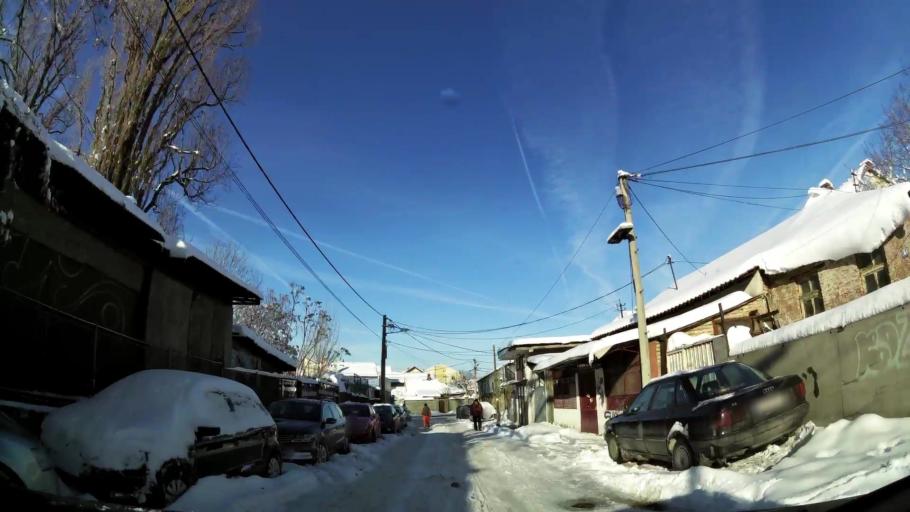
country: RS
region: Central Serbia
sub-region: Belgrade
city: Vracar
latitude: 44.7896
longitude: 20.4897
